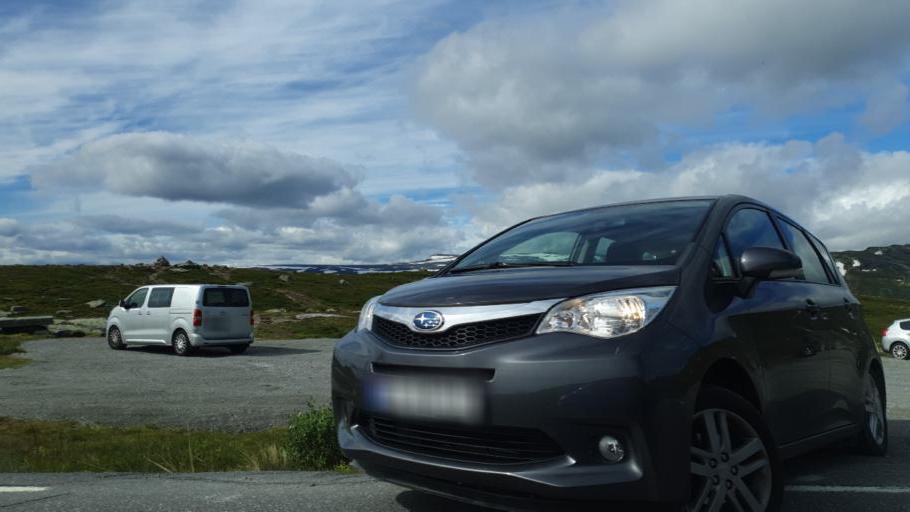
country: NO
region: Oppland
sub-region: Vestre Slidre
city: Slidre
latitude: 61.2838
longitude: 8.8299
